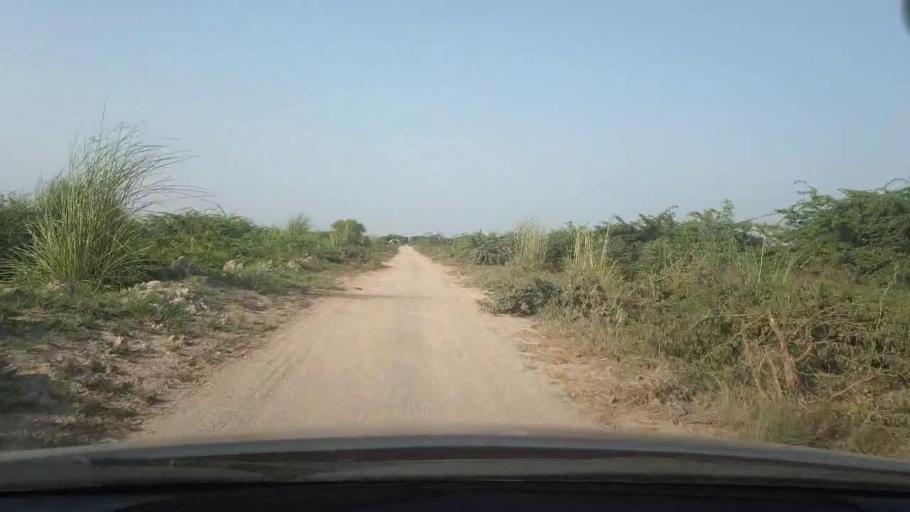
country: PK
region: Sindh
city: Naukot
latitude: 24.7756
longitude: 69.2323
